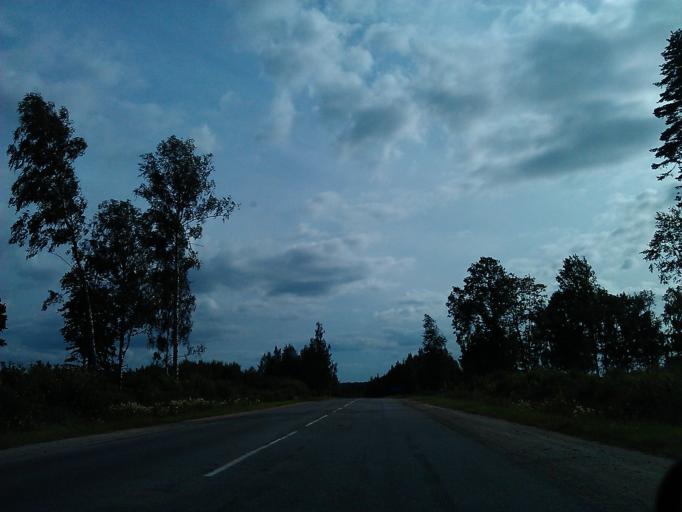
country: LV
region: Amatas Novads
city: Drabesi
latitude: 57.2706
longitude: 25.2765
